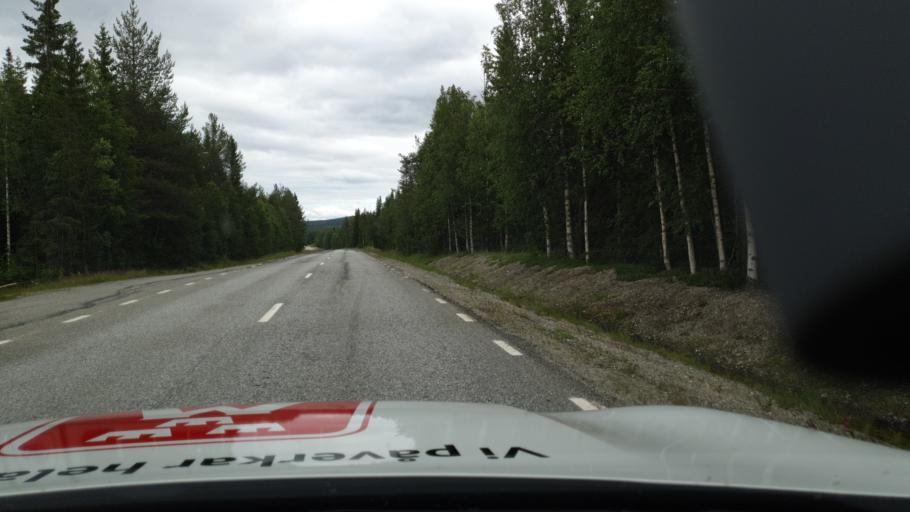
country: SE
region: Vaesterbotten
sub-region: Lycksele Kommun
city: Soderfors
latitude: 64.6361
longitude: 17.8993
